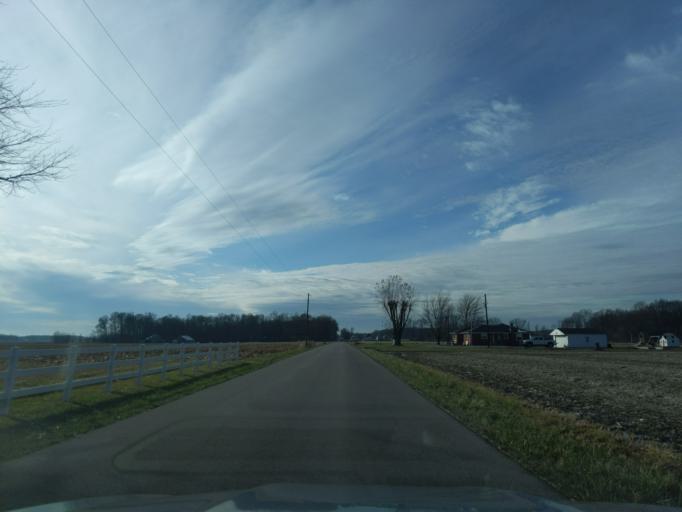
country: US
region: Indiana
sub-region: Decatur County
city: Westport
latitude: 39.1901
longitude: -85.4819
